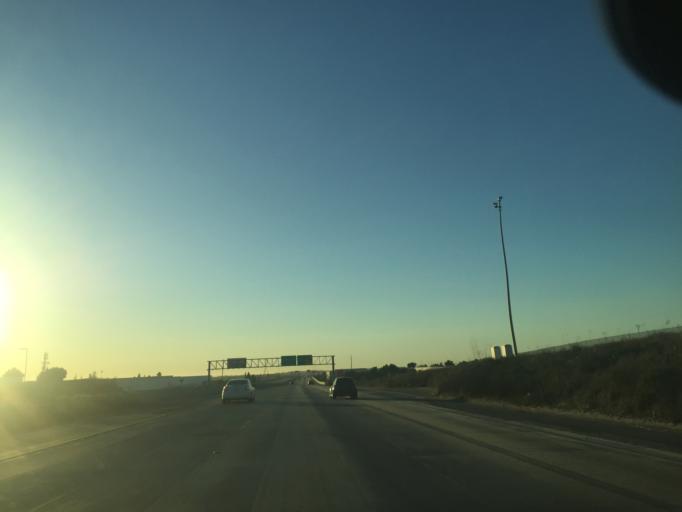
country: MX
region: Baja California
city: Tijuana
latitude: 32.5640
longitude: -116.9340
